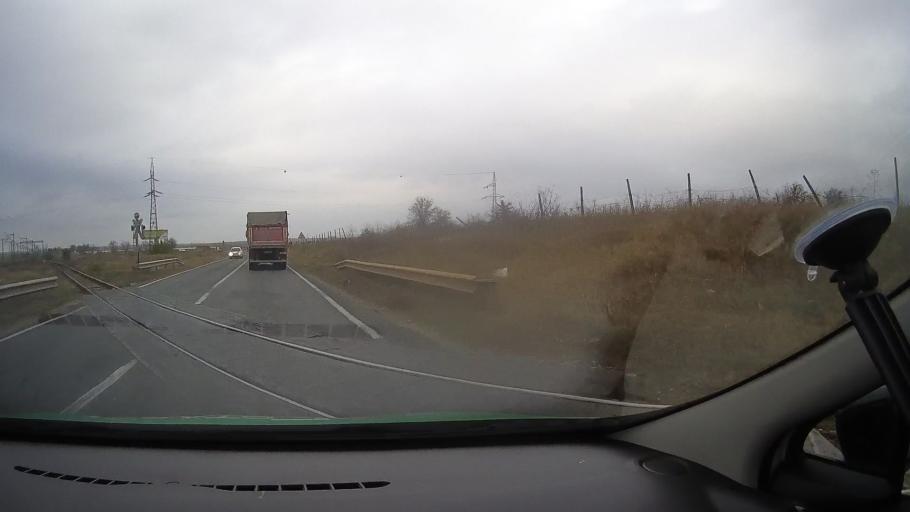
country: RO
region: Constanta
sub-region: Comuna Poarta Alba
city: Poarta Alba
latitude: 44.2331
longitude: 28.3767
